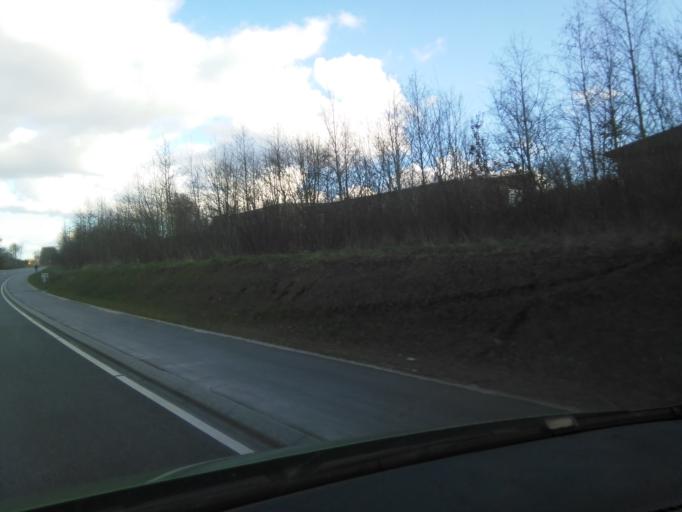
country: DK
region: Central Jutland
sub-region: Silkeborg Kommune
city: Silkeborg
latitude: 56.1893
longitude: 9.4984
